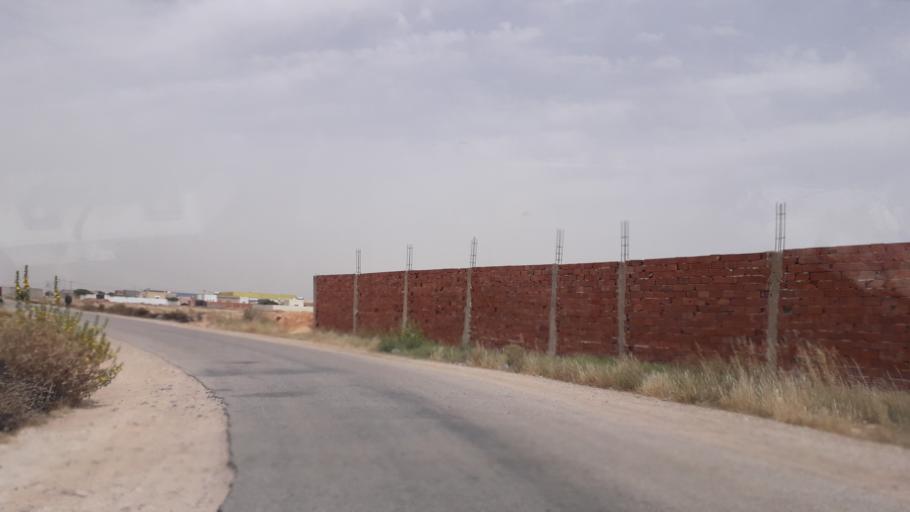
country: TN
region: Safaqis
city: Al Qarmadah
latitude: 34.8452
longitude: 10.7563
